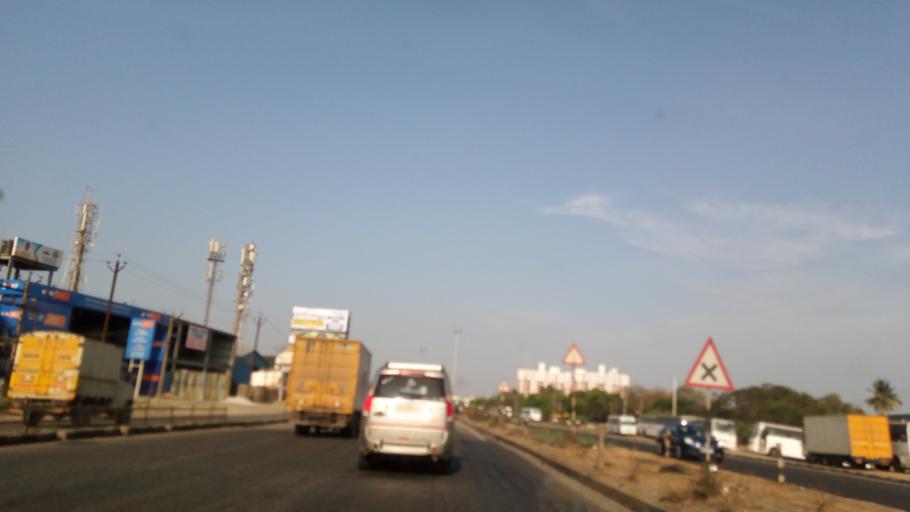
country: IN
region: Tamil Nadu
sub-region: Kancheepuram
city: Poonamalle
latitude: 13.0564
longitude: 80.0961
